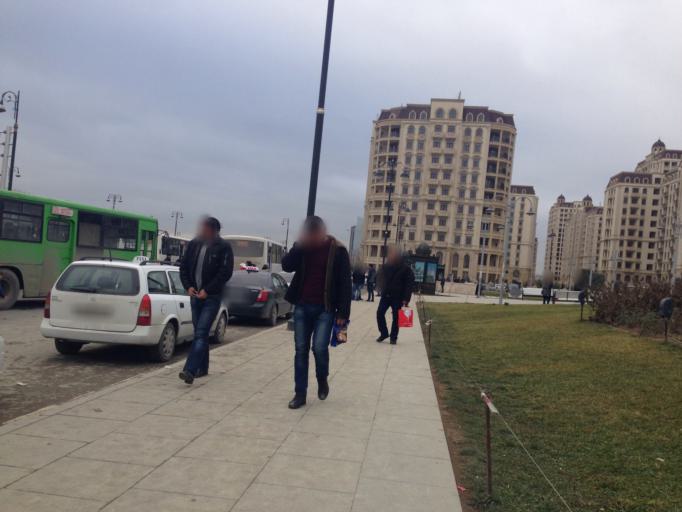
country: AZ
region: Baki
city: Sabuncu
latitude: 40.4219
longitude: 49.9174
